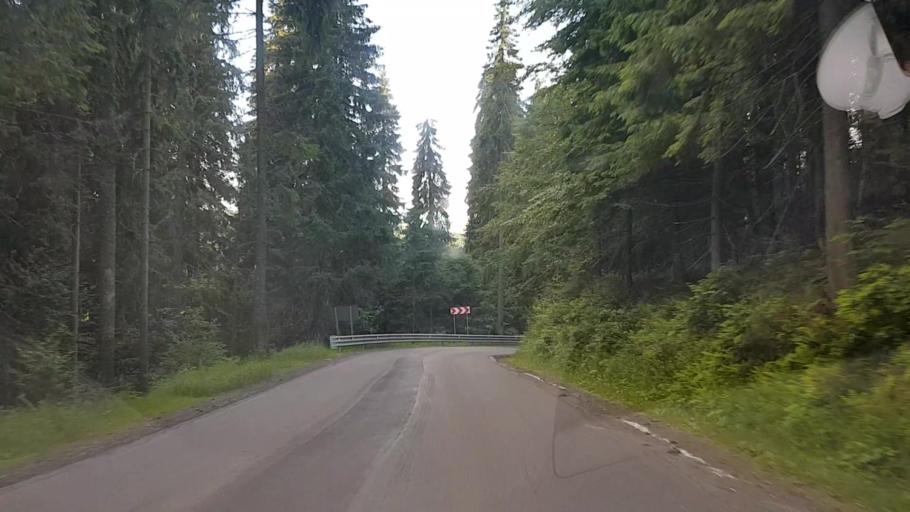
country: RO
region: Harghita
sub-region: Comuna Varsag
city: Varsag
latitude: 46.6472
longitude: 25.2877
